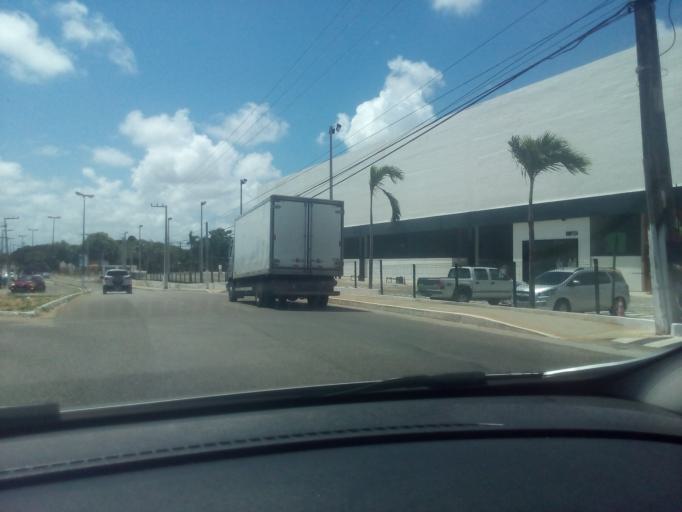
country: BR
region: Rio Grande do Norte
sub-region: Parnamirim
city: Parnamirim
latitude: -5.8960
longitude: -35.1980
